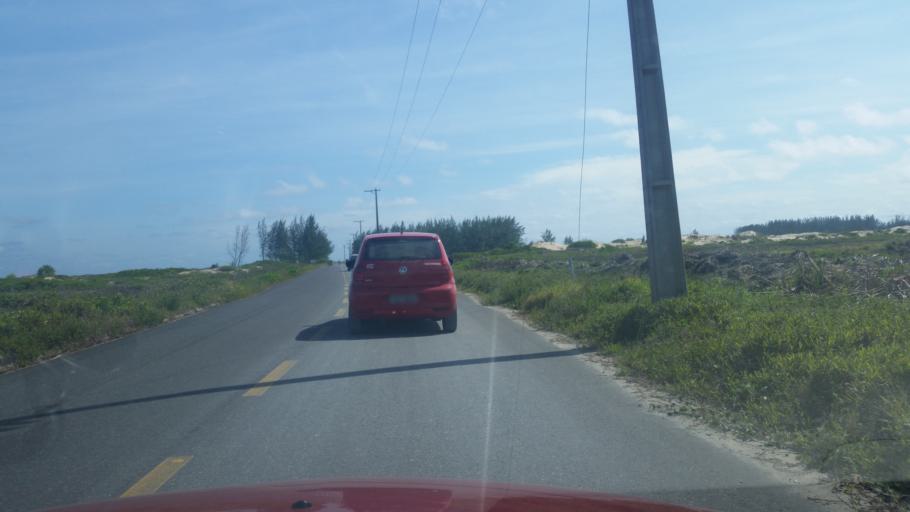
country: BR
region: Sao Paulo
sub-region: Iguape
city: Iguape
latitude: -24.7040
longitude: -47.4703
